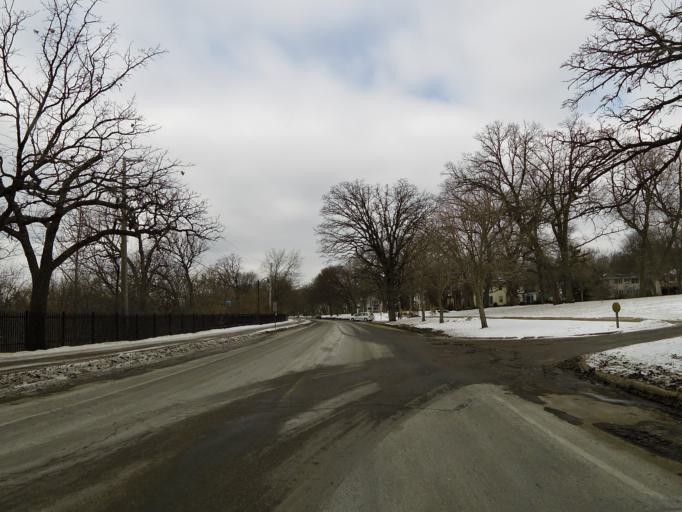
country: US
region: Minnesota
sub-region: Ramsey County
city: Lauderdale
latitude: 44.9581
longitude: -93.2121
